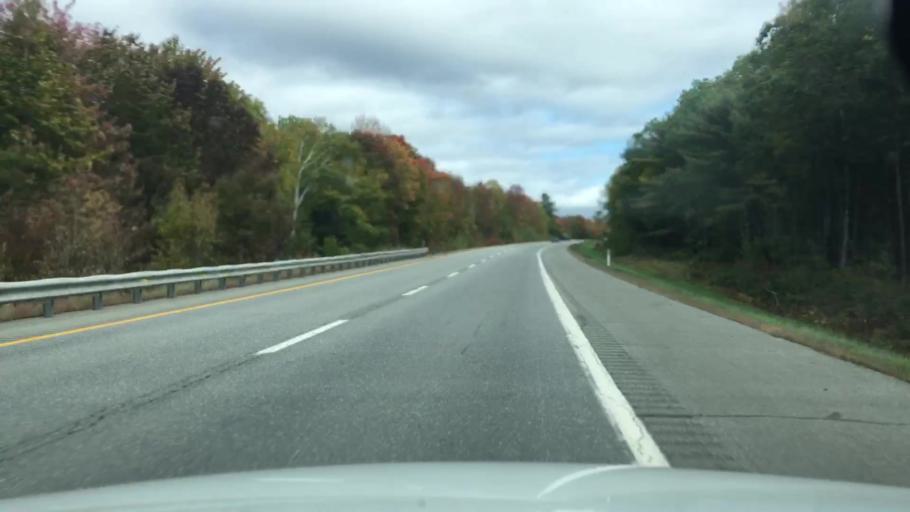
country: US
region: Maine
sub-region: Penobscot County
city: Carmel
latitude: 44.7731
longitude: -69.0154
